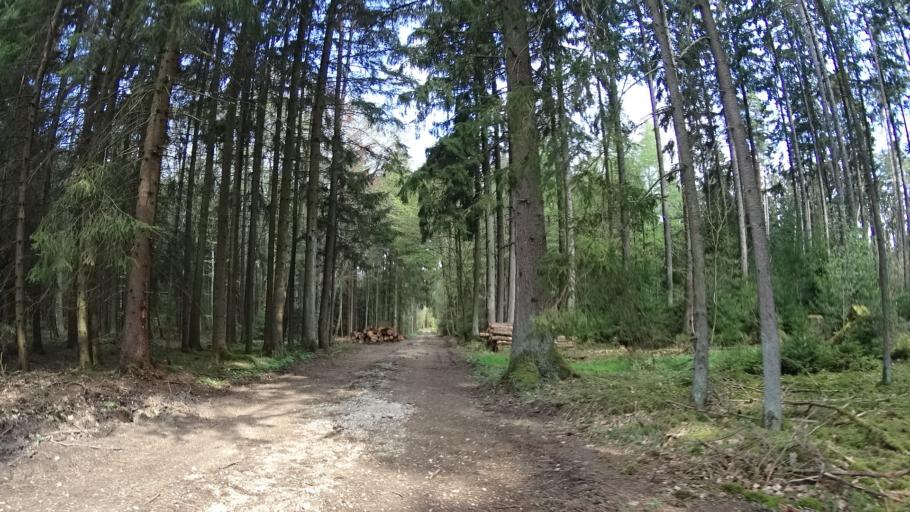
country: DE
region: Bavaria
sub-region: Upper Bavaria
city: Wettstetten
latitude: 48.8503
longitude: 11.4067
